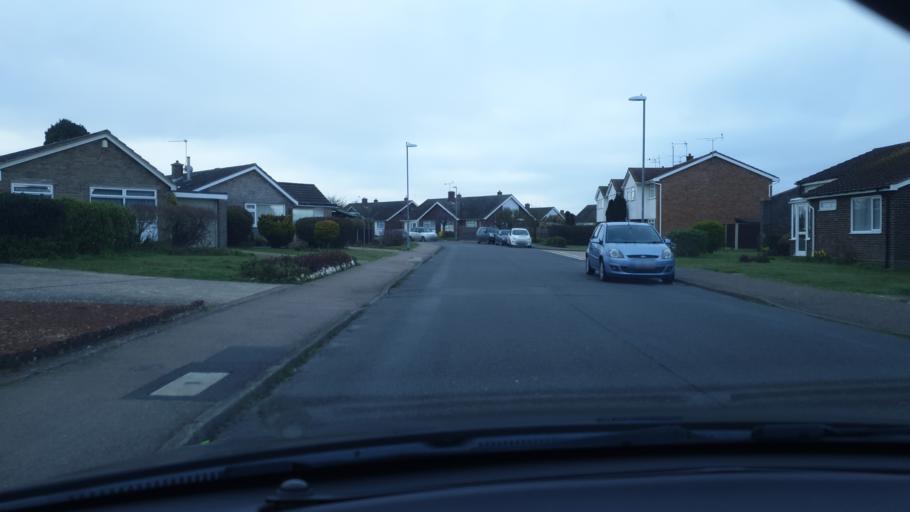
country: GB
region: England
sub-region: Essex
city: Walton-on-the-Naze
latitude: 51.8465
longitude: 1.2509
